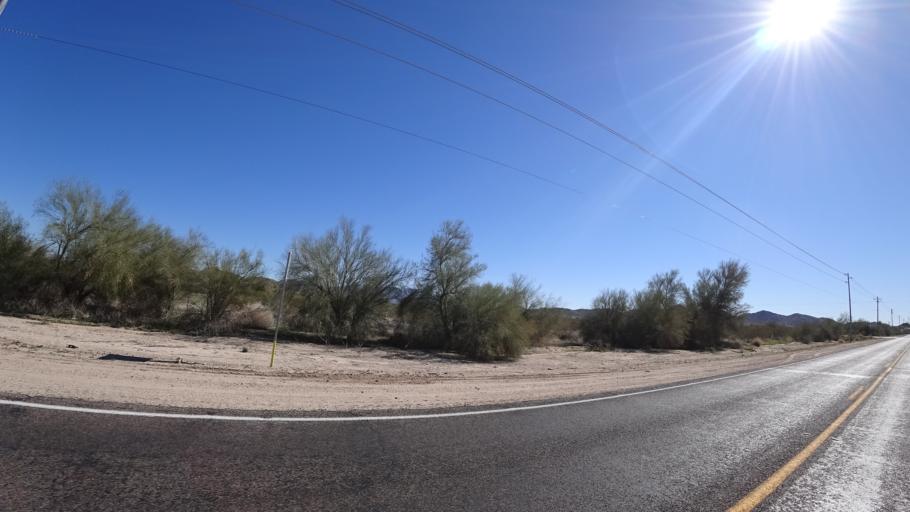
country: US
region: Arizona
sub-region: Maricopa County
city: Buckeye
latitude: 33.3355
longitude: -112.4699
